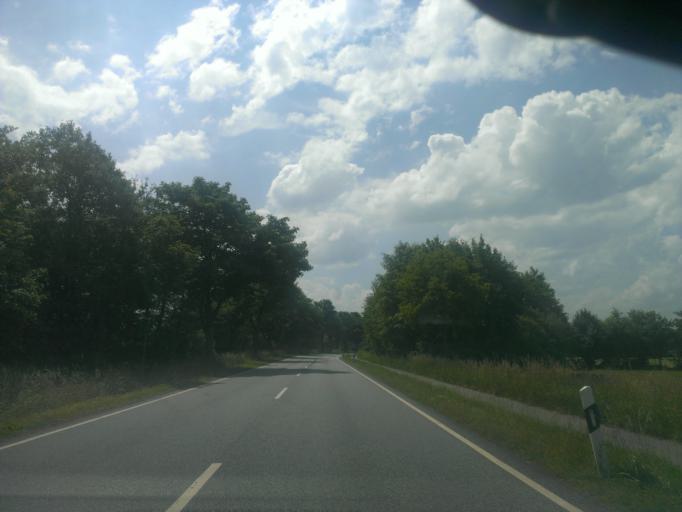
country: DE
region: Schleswig-Holstein
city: Fockbek
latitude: 54.2855
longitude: 9.5786
